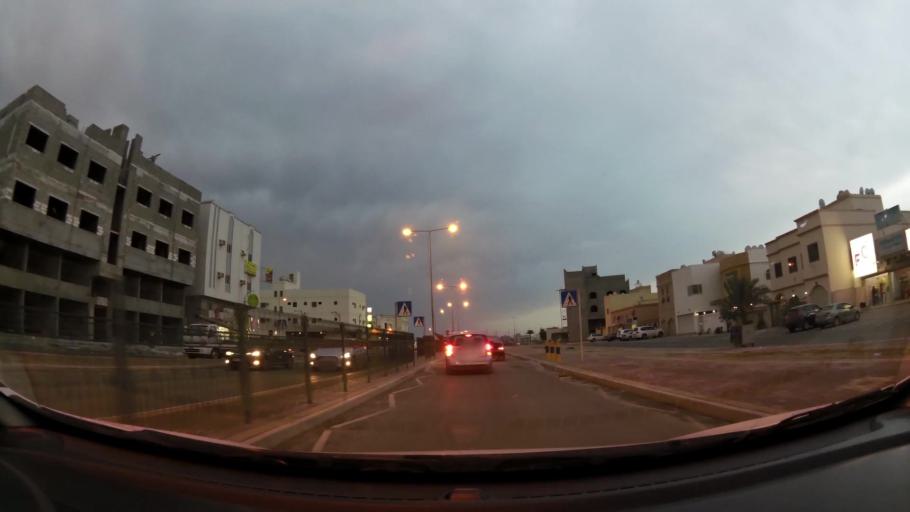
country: BH
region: Central Governorate
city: Madinat Hamad
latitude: 26.1543
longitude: 50.5099
